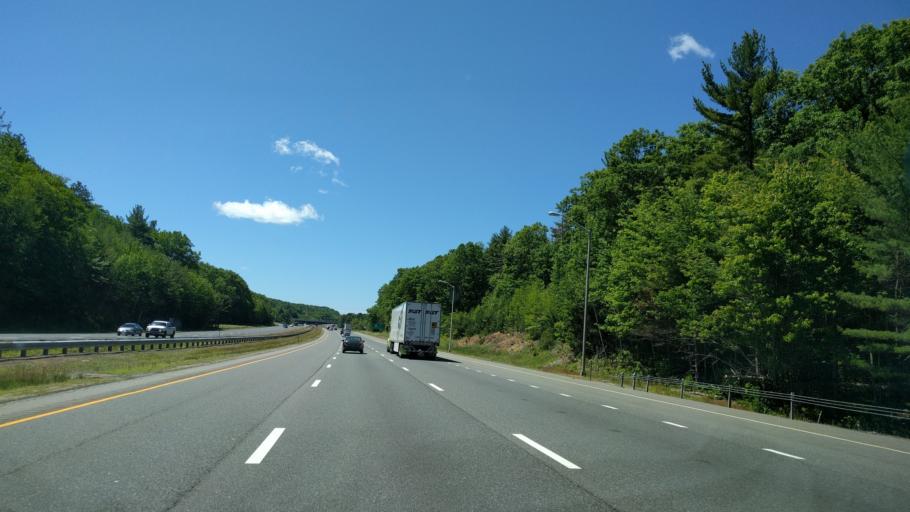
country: US
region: Massachusetts
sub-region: Hampden County
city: Holland
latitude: 41.9835
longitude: -72.1779
